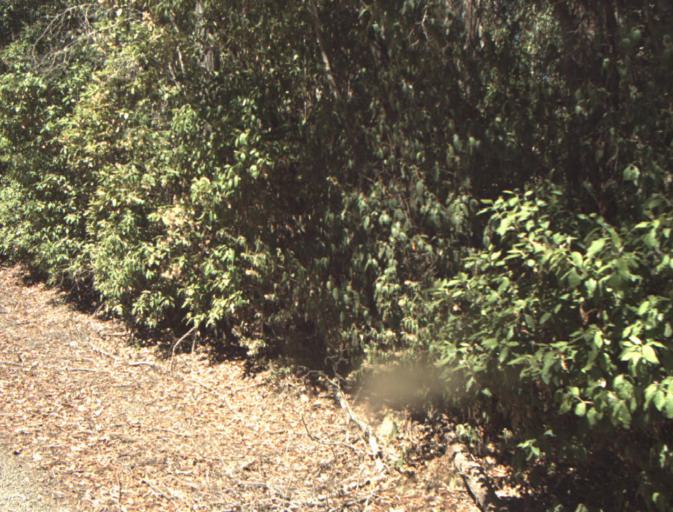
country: AU
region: Tasmania
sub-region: Dorset
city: Scottsdale
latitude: -41.3533
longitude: 147.3890
